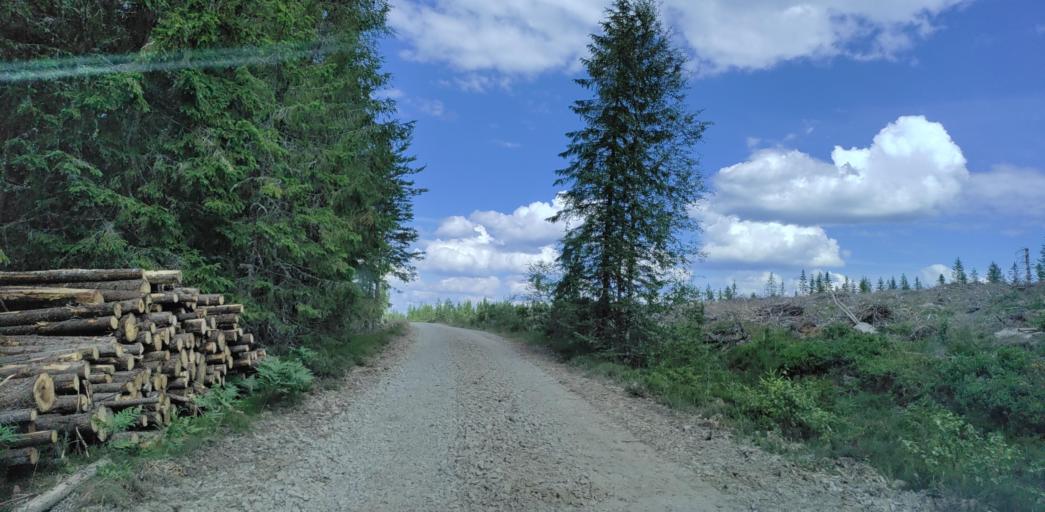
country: SE
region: Vaermland
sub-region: Hagfors Kommun
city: Ekshaerad
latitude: 60.0677
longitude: 13.3422
